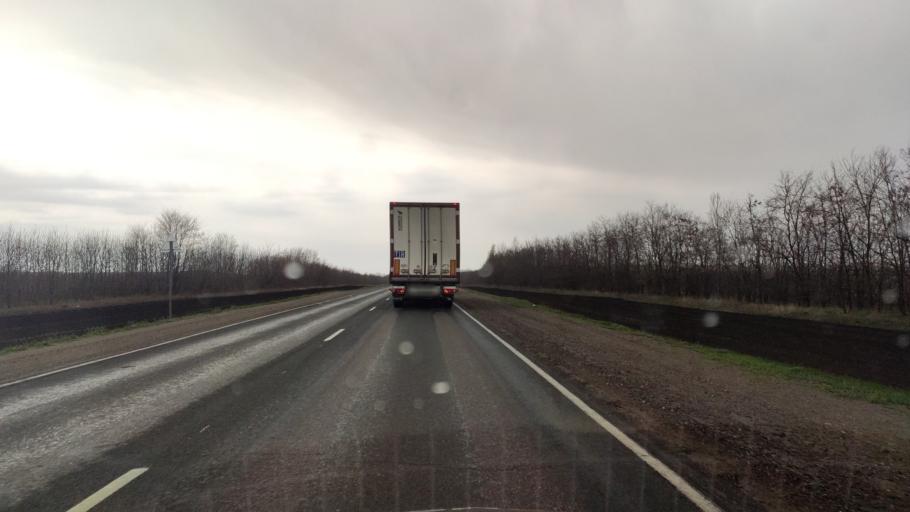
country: RU
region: Voronezj
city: Nizhnedevitsk
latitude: 51.5695
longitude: 38.3368
